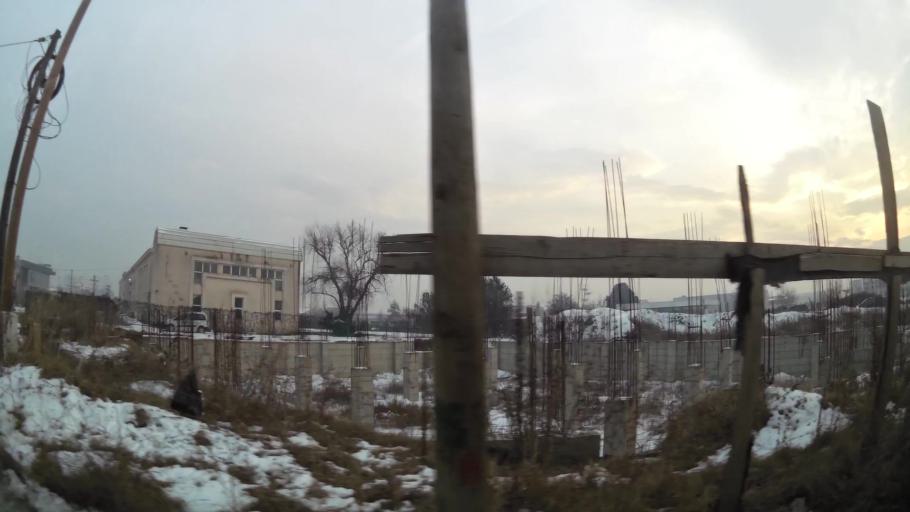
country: MK
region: Suto Orizari
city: Suto Orizare
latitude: 42.0339
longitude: 21.4026
